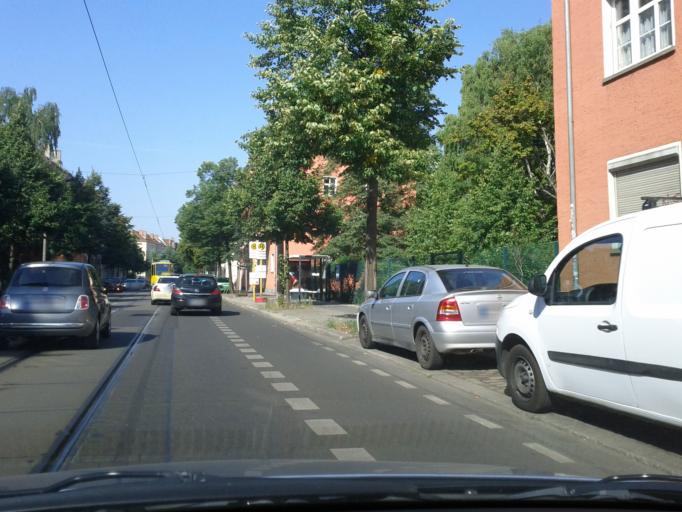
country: DE
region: Berlin
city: Berlin Koepenick
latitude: 52.4555
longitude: 13.5856
